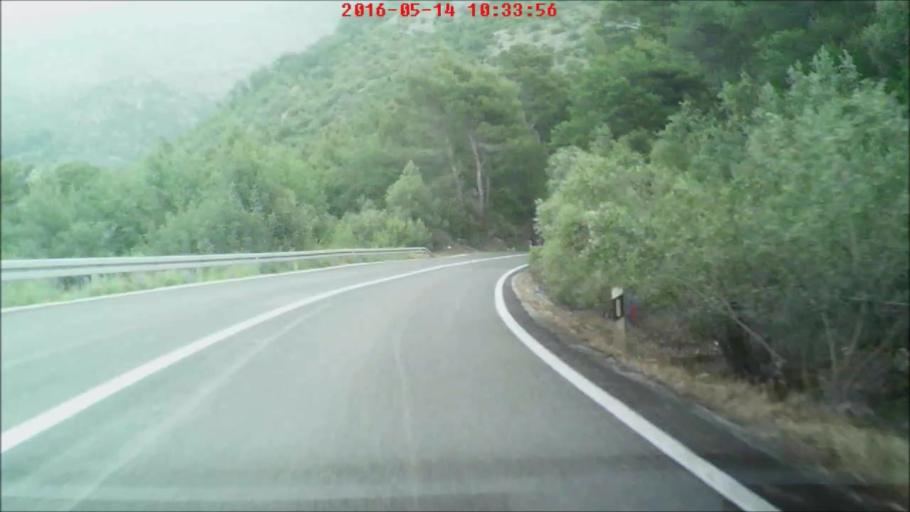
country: HR
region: Dubrovacko-Neretvanska
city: Podgora
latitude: 42.7780
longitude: 17.8871
